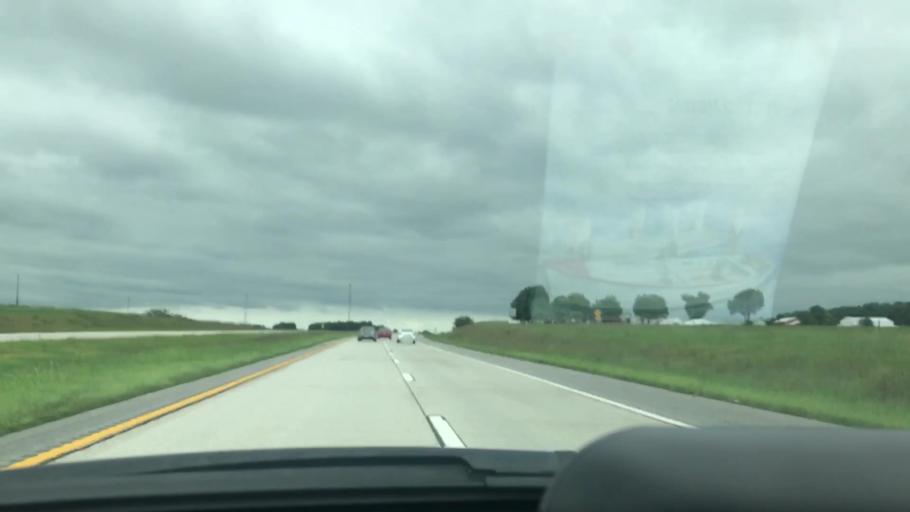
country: US
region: Missouri
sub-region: Greene County
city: Fair Grove
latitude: 37.4430
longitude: -93.1442
